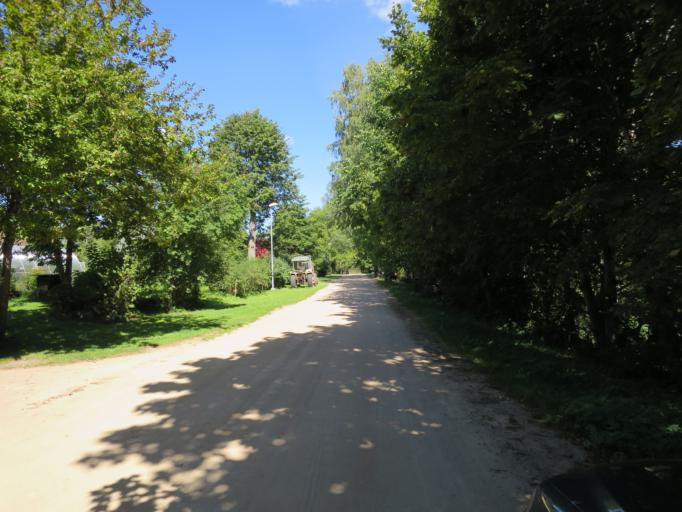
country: LV
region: Malpils
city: Malpils
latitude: 57.0086
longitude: 24.9666
